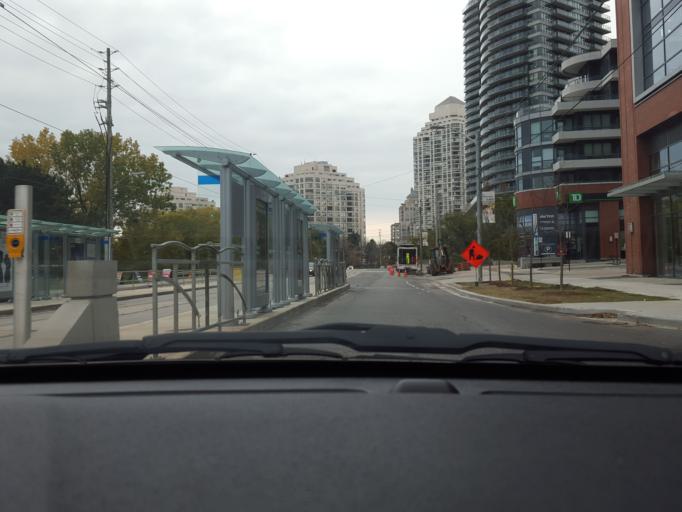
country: CA
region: Ontario
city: Etobicoke
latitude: 43.6230
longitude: -79.4814
